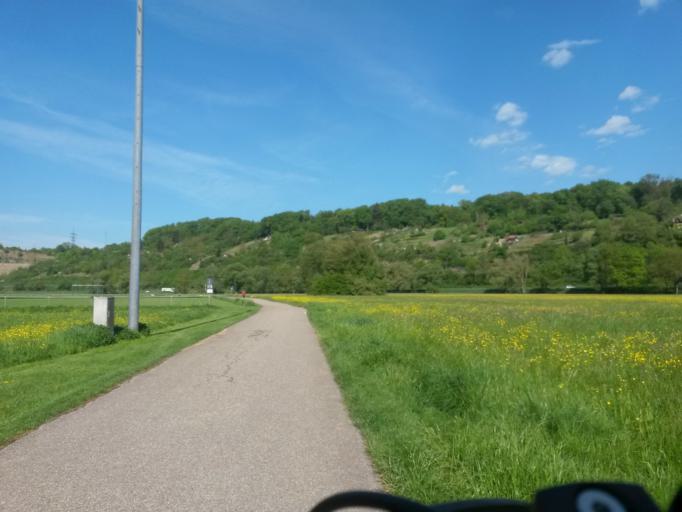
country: DE
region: Baden-Wuerttemberg
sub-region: Karlsruhe Region
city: Muhlacker
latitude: 48.9462
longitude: 8.8281
